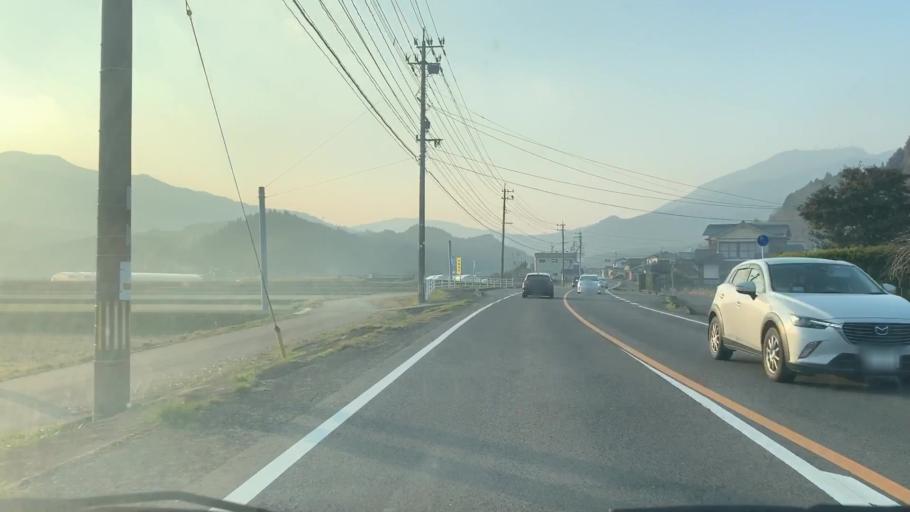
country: JP
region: Saga Prefecture
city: Takeocho-takeo
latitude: 33.2586
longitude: 130.0685
